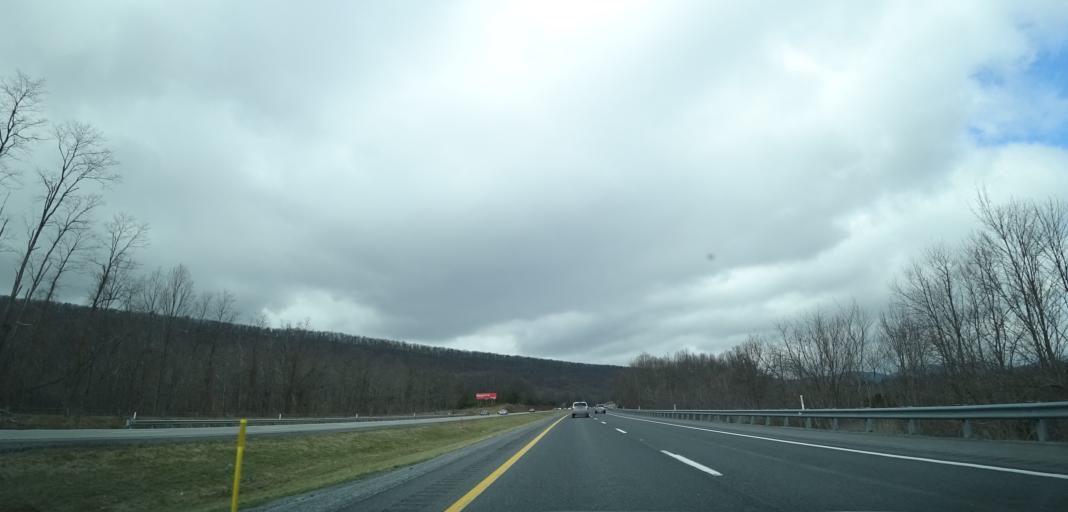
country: US
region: Maryland
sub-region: Washington County
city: Hancock
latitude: 39.8337
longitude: -78.2752
